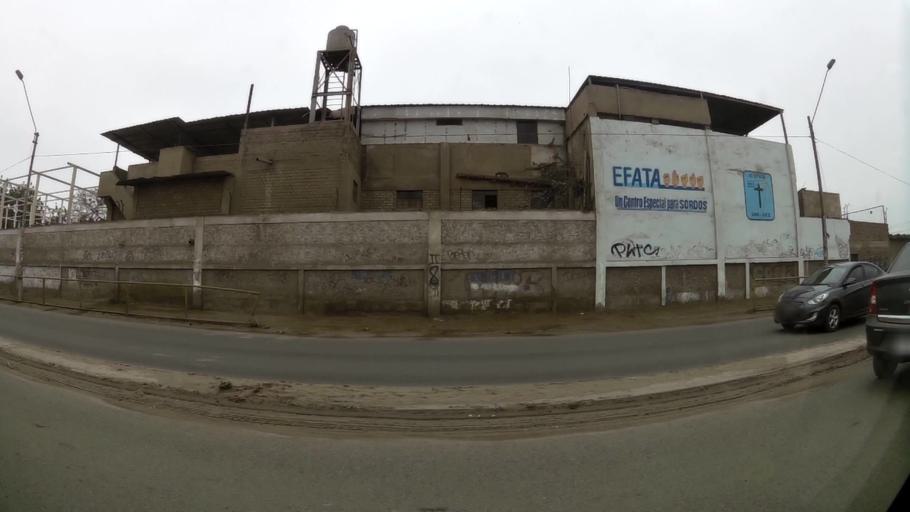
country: PE
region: Lima
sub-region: Lima
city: Surco
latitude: -12.2014
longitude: -76.9439
